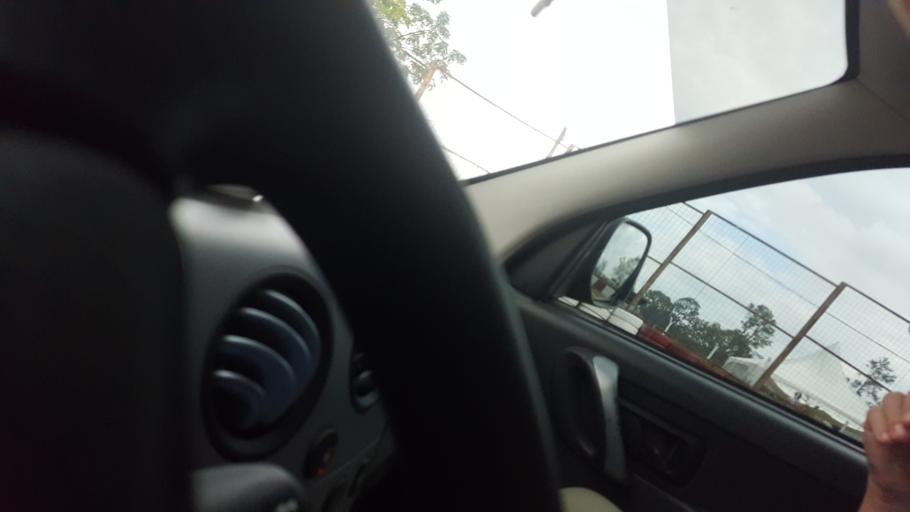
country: AR
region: Misiones
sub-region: Departamento de Capital
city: Posadas
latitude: -27.4355
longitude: -55.9278
